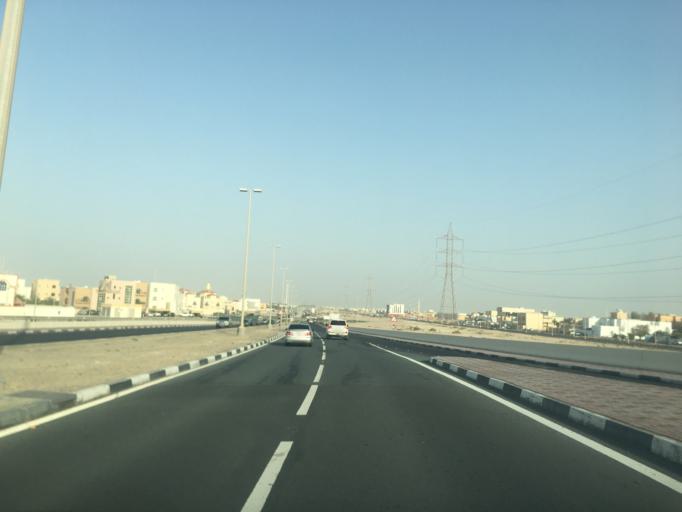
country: AE
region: Abu Dhabi
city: Abu Dhabi
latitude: 24.3247
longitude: 54.6247
